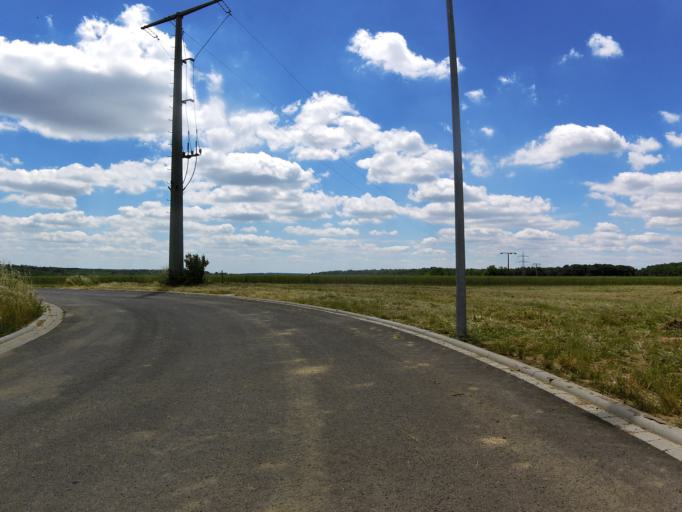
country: DE
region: Bavaria
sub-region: Regierungsbezirk Unterfranken
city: Kist
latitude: 49.7378
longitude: 9.8410
